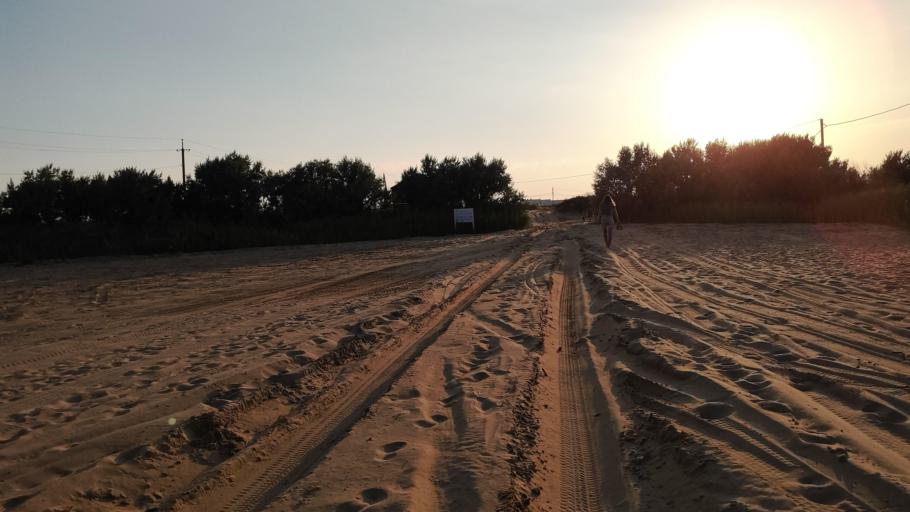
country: RU
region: Krasnodarskiy
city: Blagovetschenskaya
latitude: 45.0666
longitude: 37.0399
